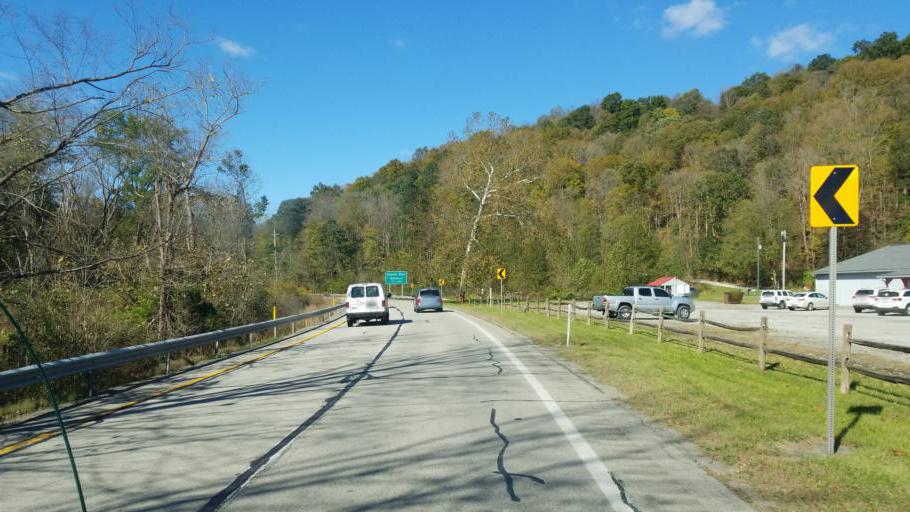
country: US
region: Pennsylvania
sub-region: Westmoreland County
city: Ligonier
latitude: 40.2593
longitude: -79.2635
